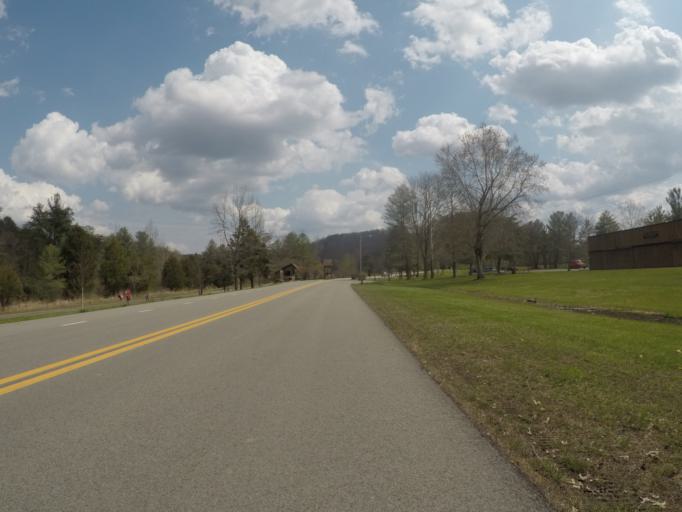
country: US
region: West Virginia
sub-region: Wayne County
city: Lavalette
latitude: 38.3084
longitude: -82.3468
